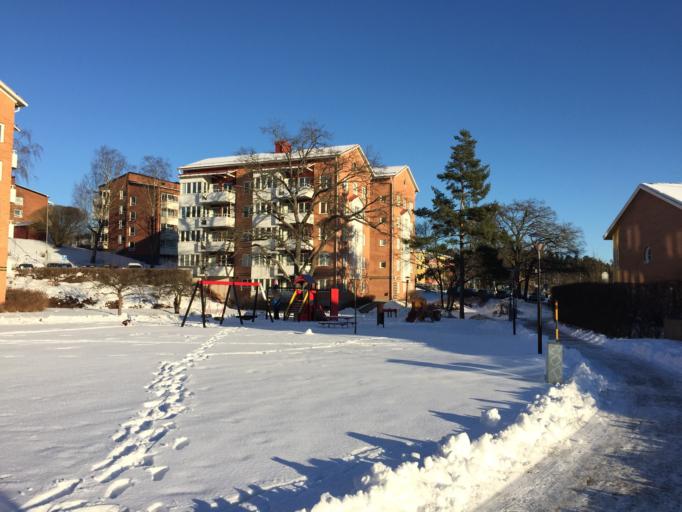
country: SE
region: Stockholm
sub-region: Salems Kommun
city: Ronninge
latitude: 59.1946
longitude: 17.7471
